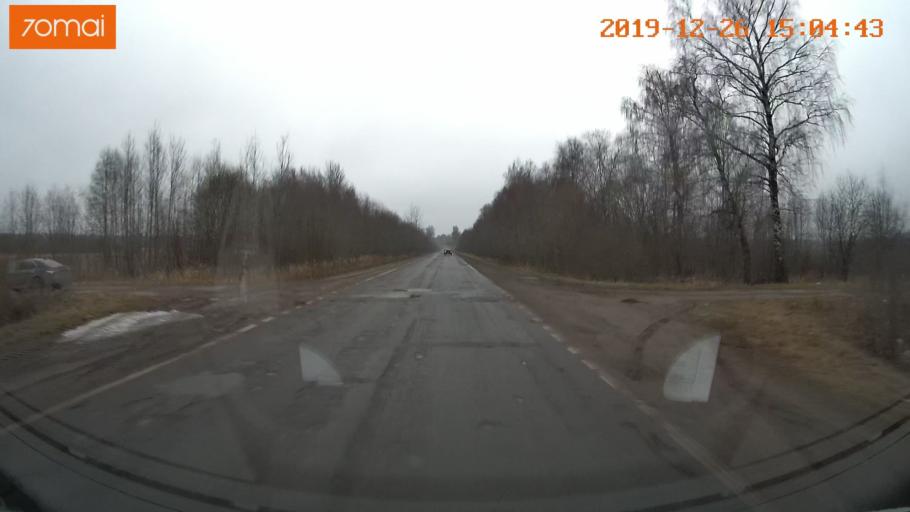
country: RU
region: Jaroslavl
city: Rybinsk
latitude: 58.1968
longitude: 38.8587
